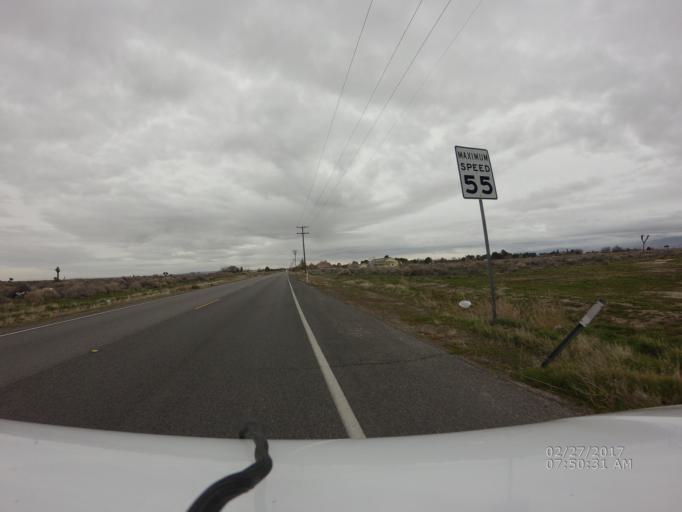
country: US
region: California
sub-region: Los Angeles County
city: Lancaster
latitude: 34.7046
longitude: -118.0584
